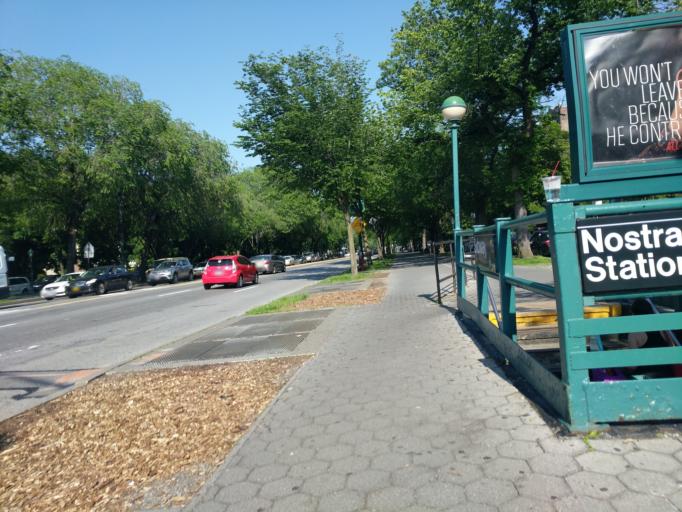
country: US
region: New York
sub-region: Kings County
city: Brooklyn
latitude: 40.6697
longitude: -73.9503
